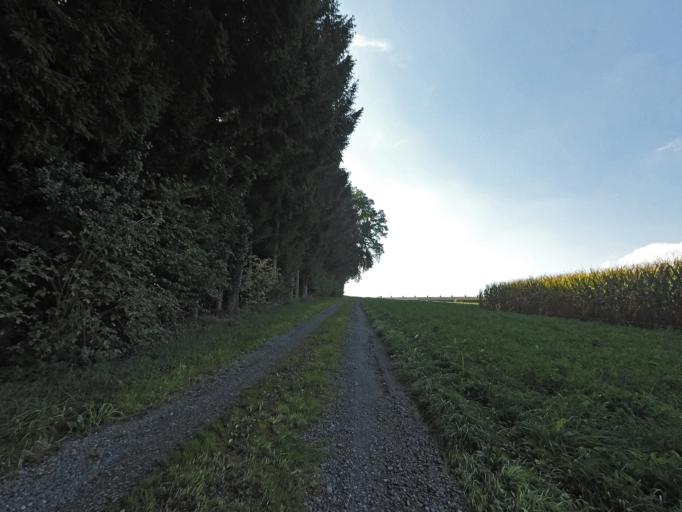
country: CH
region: Thurgau
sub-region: Frauenfeld District
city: Diessenhofen
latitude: 47.6553
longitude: 8.7363
